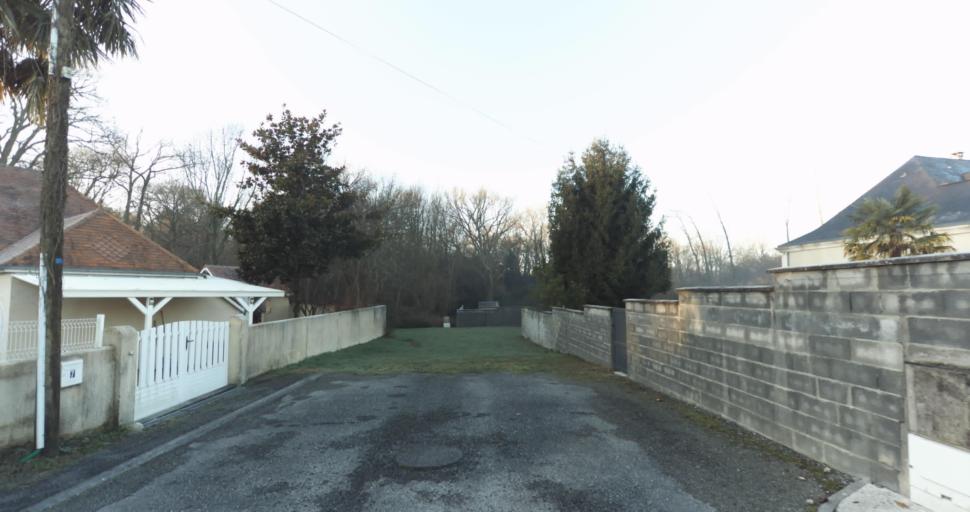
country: FR
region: Aquitaine
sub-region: Departement des Pyrenees-Atlantiques
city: Buros
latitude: 43.3268
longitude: -0.2889
